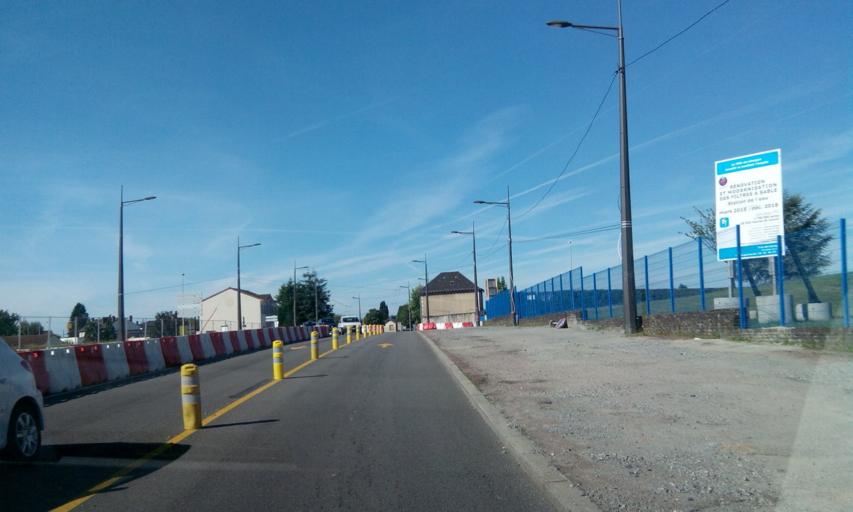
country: FR
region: Limousin
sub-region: Departement de la Haute-Vienne
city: Limoges
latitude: 45.8563
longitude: 1.2681
